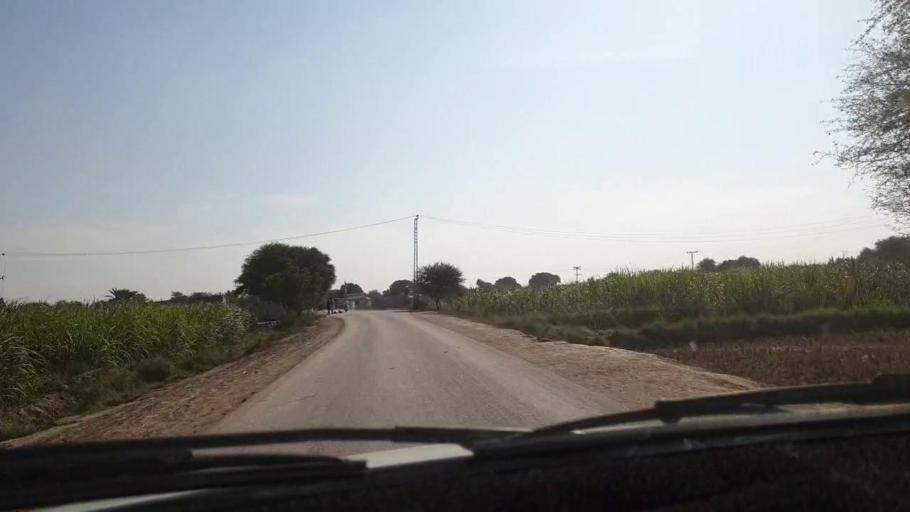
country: PK
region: Sindh
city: Bulri
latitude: 24.9585
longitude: 68.4195
